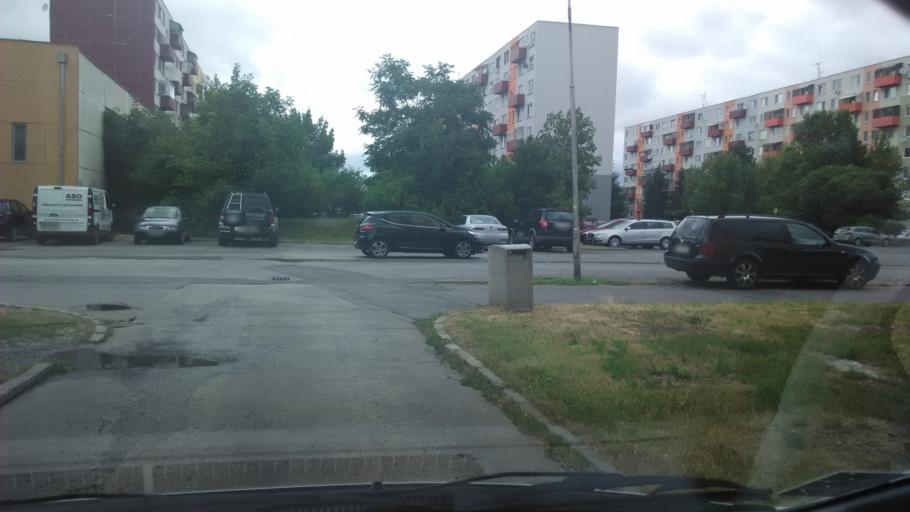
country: SK
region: Nitriansky
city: Levice
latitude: 48.2038
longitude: 18.6101
